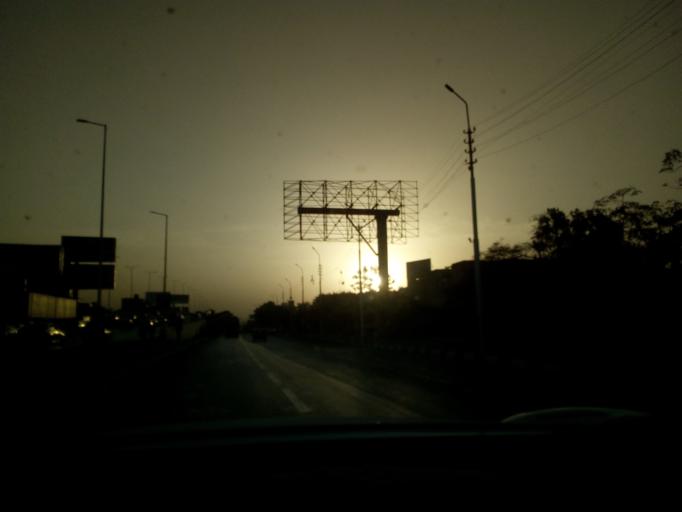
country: EG
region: Muhafazat al Qahirah
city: Cairo
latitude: 30.0968
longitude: 31.3445
